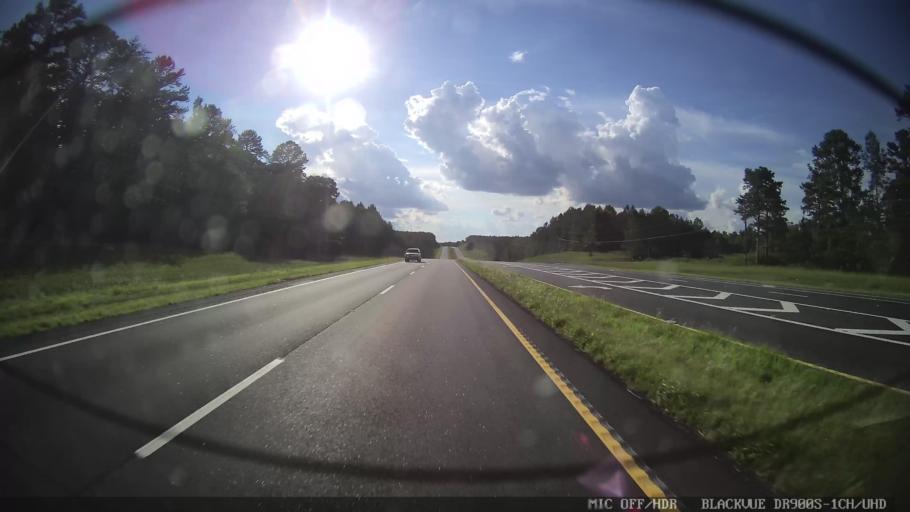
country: US
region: Georgia
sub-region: Floyd County
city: Lindale
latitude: 34.2092
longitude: -85.0932
